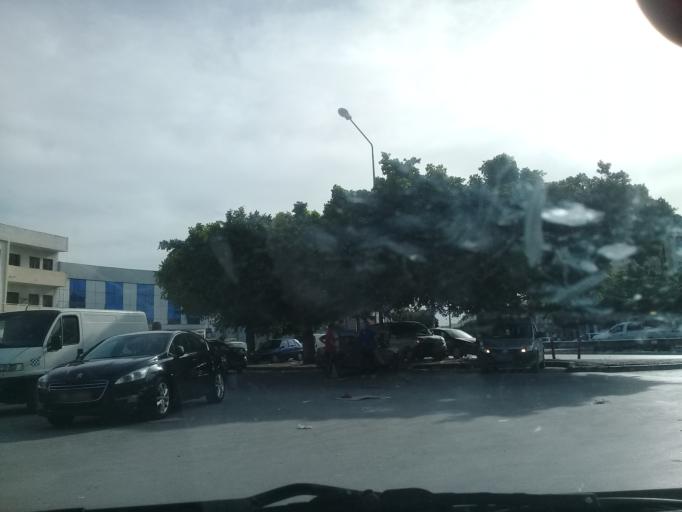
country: TN
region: Tunis
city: Tunis
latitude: 36.7928
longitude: 10.1864
